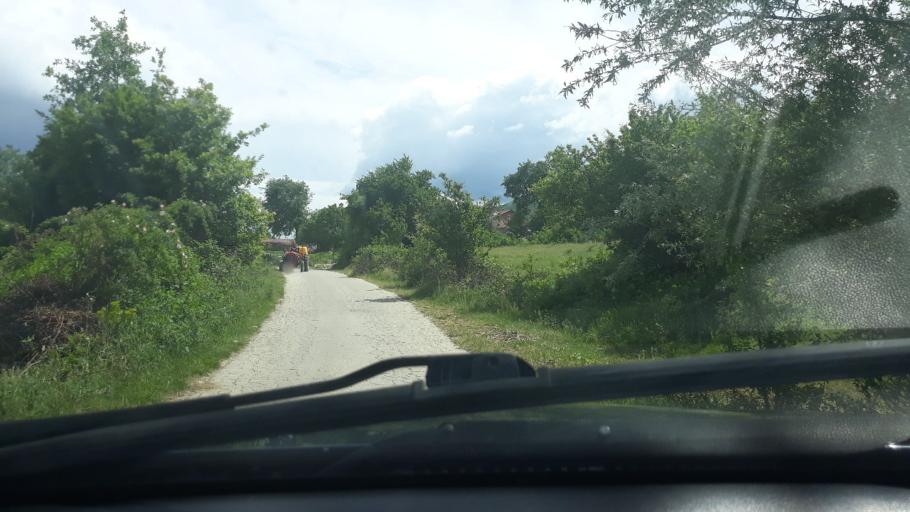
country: MK
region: Krivogastani
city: Krivogashtani
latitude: 41.3253
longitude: 21.3037
